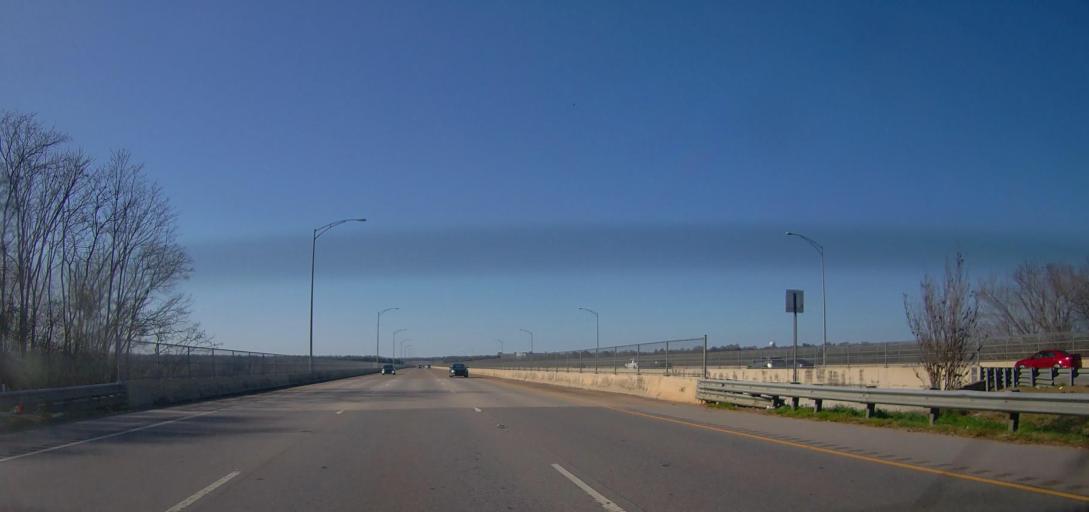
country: US
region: Alabama
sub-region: Lauderdale County
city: East Florence
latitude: 34.7904
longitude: -87.6416
